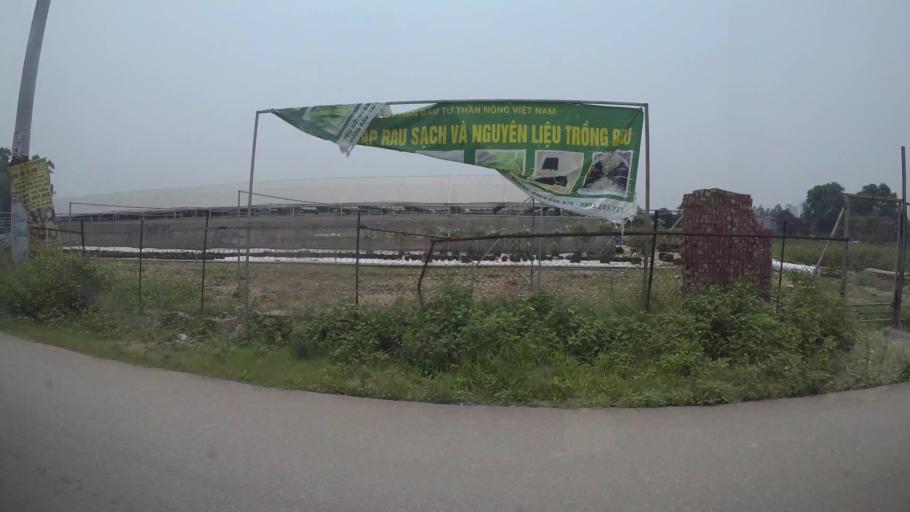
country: VN
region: Ha Noi
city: Ha Dong
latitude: 20.9976
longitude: 105.7671
